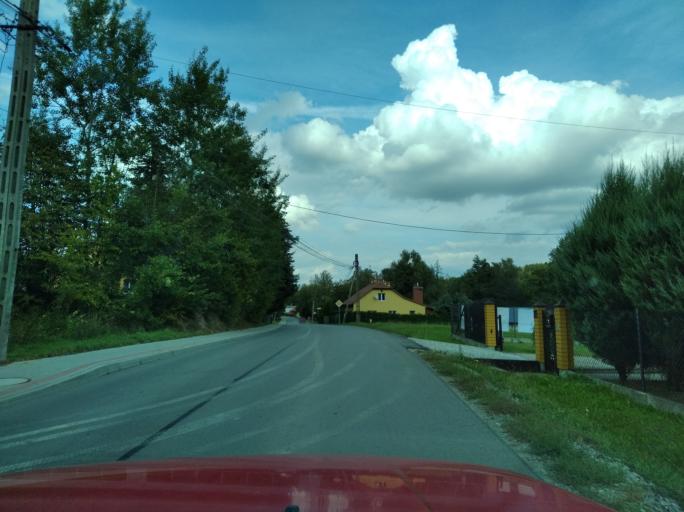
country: PL
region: Subcarpathian Voivodeship
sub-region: Powiat rzeszowski
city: Tyczyn
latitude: 49.9455
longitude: 22.0233
